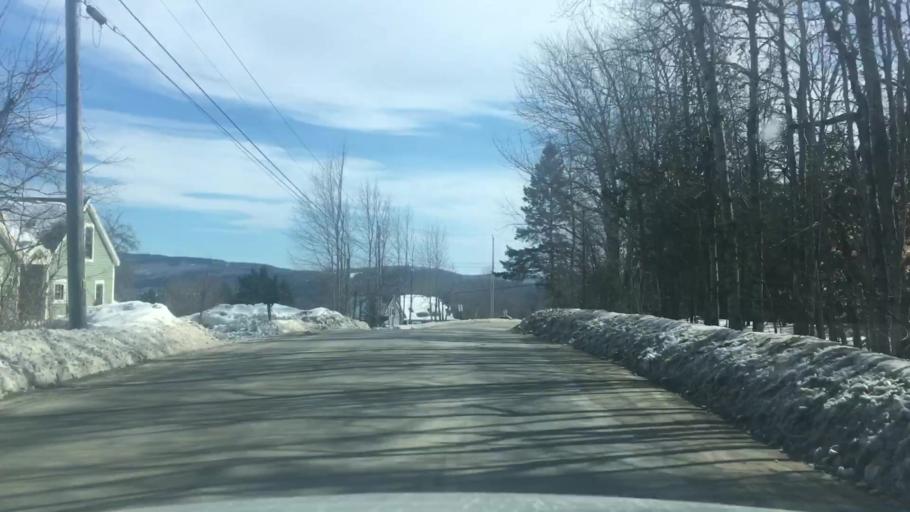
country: US
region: Maine
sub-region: Penobscot County
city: Holden
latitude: 44.7652
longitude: -68.6438
